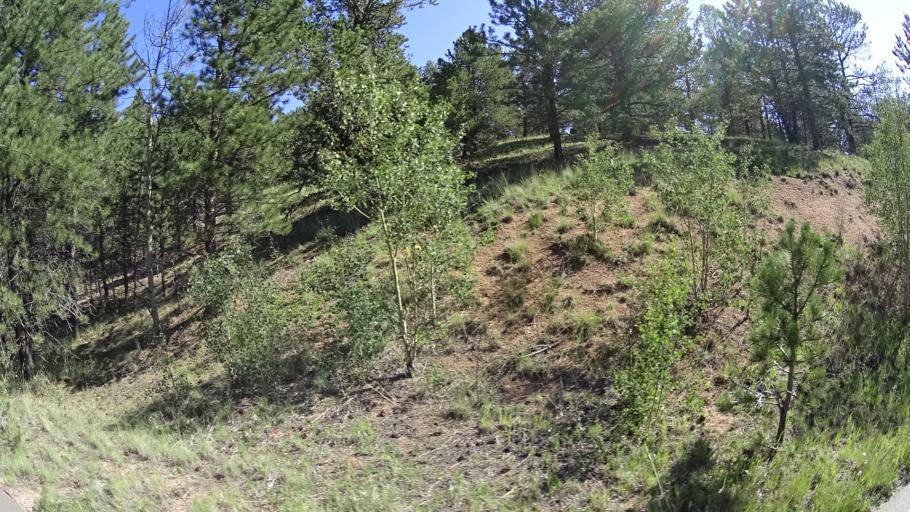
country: US
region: Colorado
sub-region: El Paso County
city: Cascade-Chipita Park
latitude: 38.9124
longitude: -105.0284
